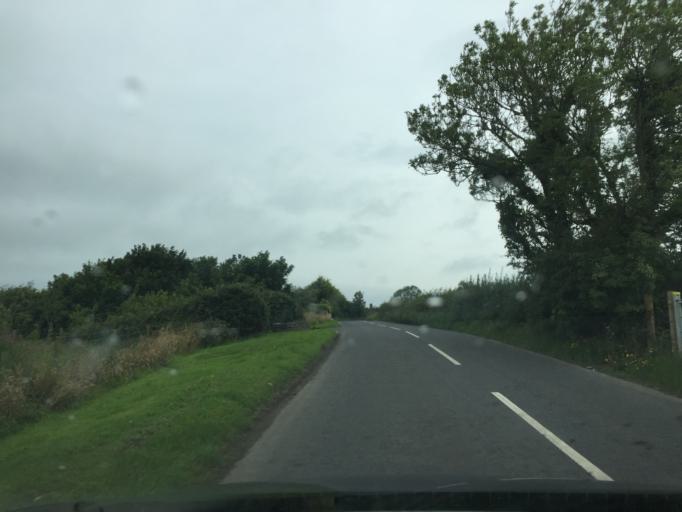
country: GB
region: Northern Ireland
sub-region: Down District
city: Kircubbin
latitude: 54.4918
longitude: -5.4955
